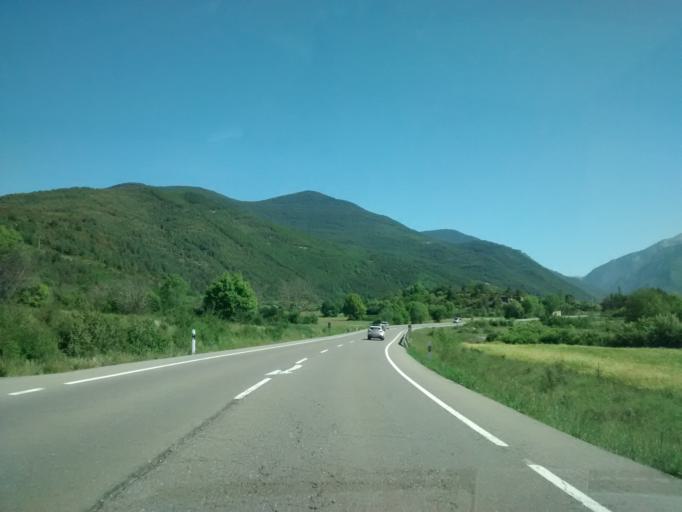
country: ES
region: Aragon
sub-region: Provincia de Huesca
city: Castiello de Jaca
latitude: 42.6521
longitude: -0.5593
